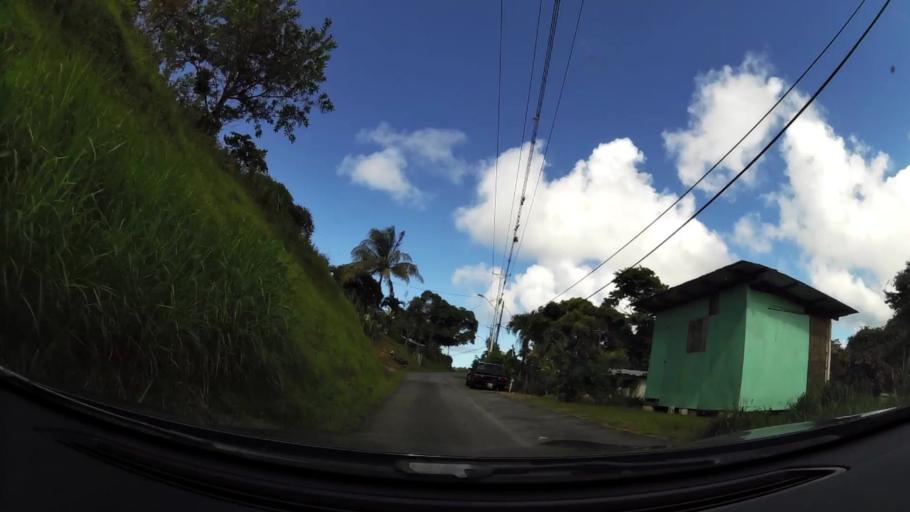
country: TT
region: Eastern Tobago
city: Roxborough
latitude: 11.3093
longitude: -60.6189
